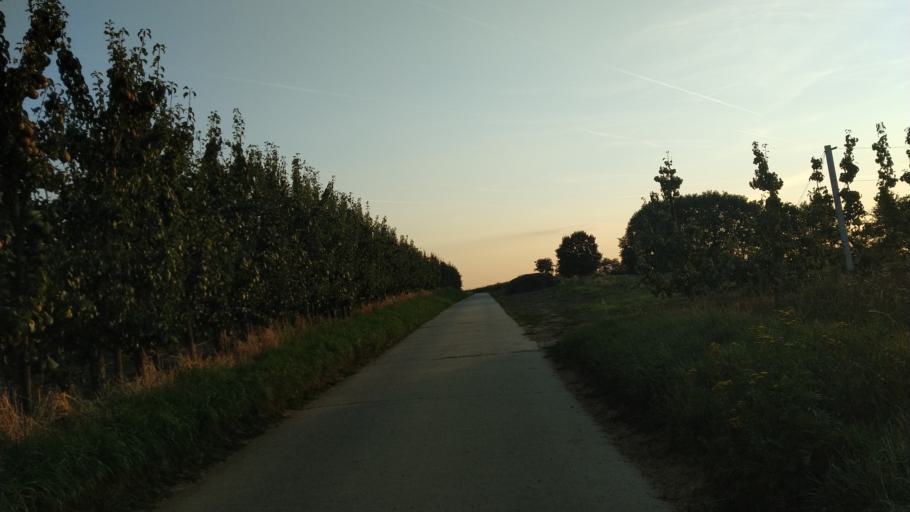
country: BE
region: Flanders
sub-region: Provincie Vlaams-Brabant
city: Lubbeek
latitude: 50.8865
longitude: 4.8165
